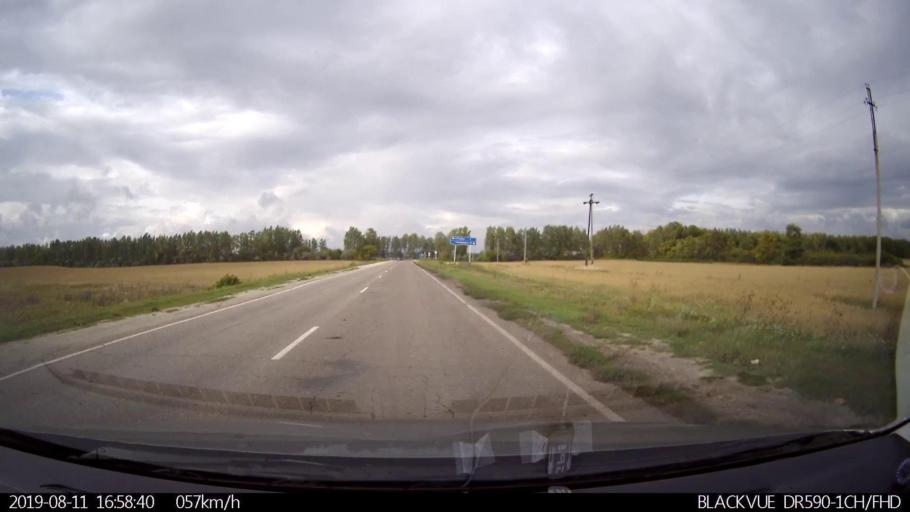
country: RU
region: Ulyanovsk
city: Mayna
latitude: 54.3102
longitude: 47.6567
